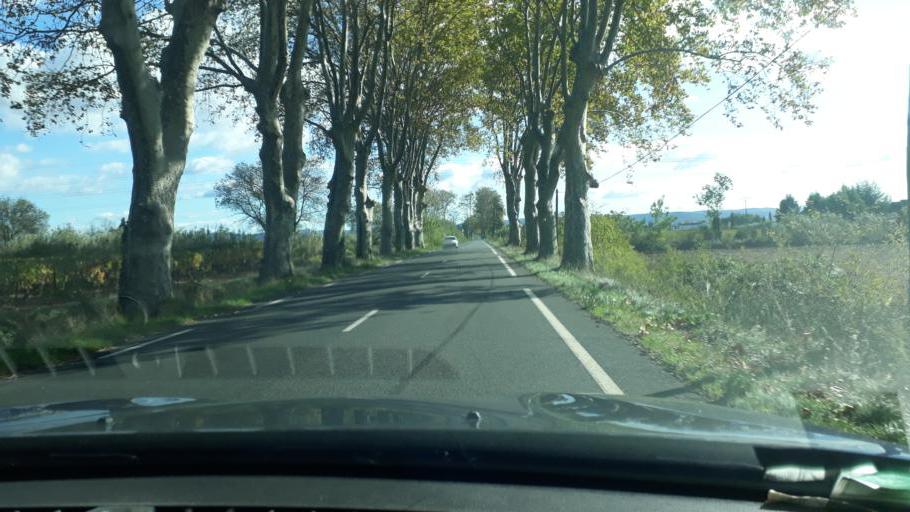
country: FR
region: Languedoc-Roussillon
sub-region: Departement de l'Herault
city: Saint-Andre-de-Sangonis
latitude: 43.6562
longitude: 3.4800
